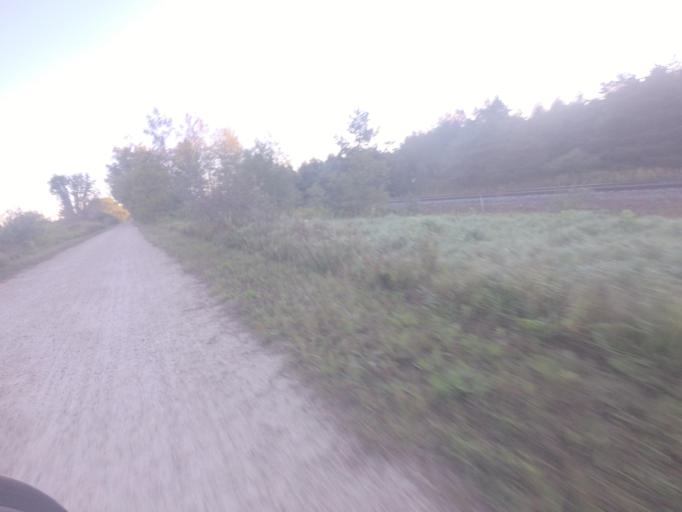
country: CA
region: Ontario
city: Bradford West Gwillimbury
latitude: 43.9711
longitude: -79.8097
